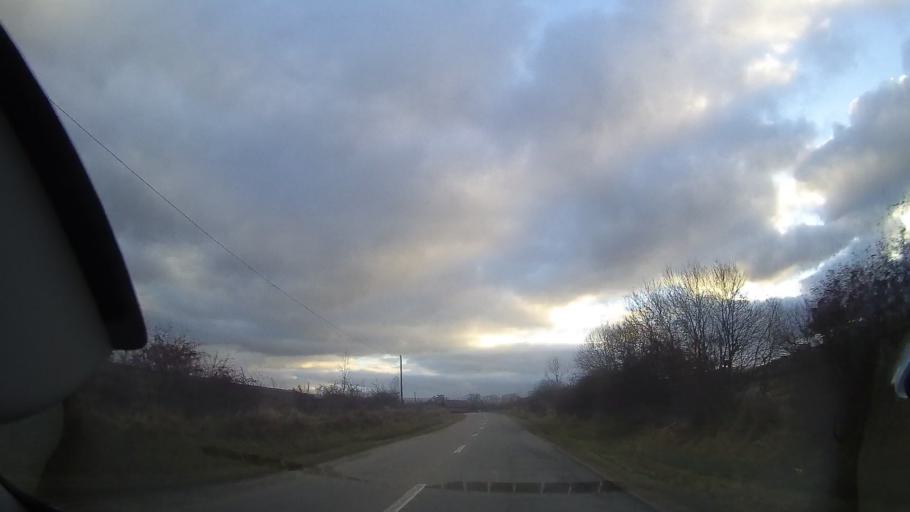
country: RO
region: Cluj
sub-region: Comuna Sancraiu
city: Sancraiu
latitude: 46.8211
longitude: 22.9942
